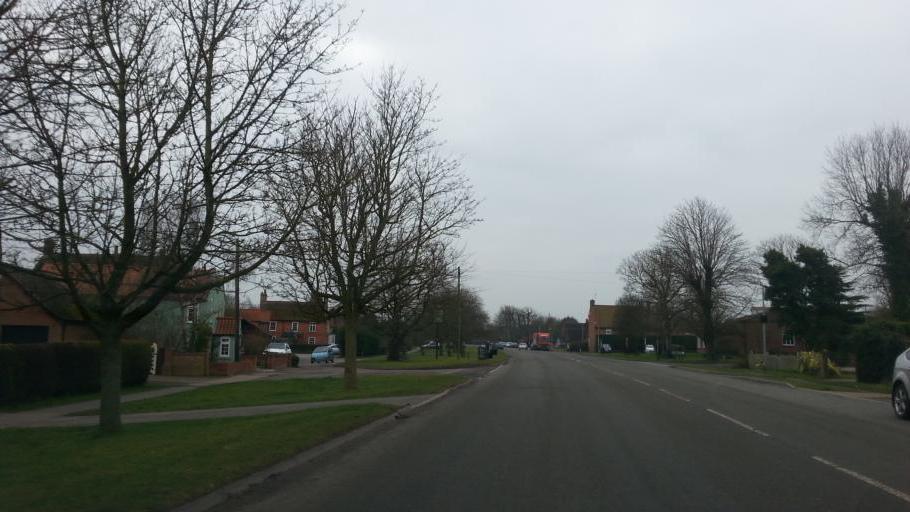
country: GB
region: England
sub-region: Lincolnshire
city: Long Bennington
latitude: 52.9955
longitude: -0.7585
